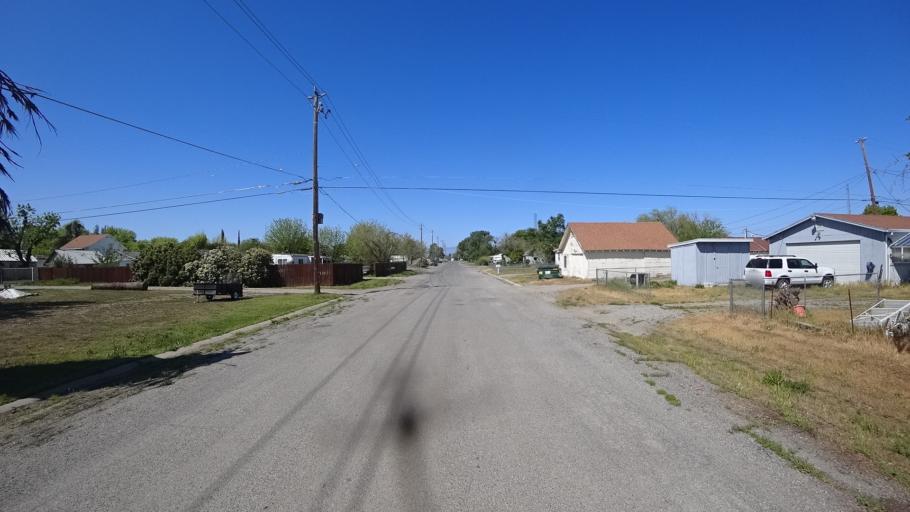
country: US
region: California
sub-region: Glenn County
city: Willows
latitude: 39.5291
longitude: -122.1885
